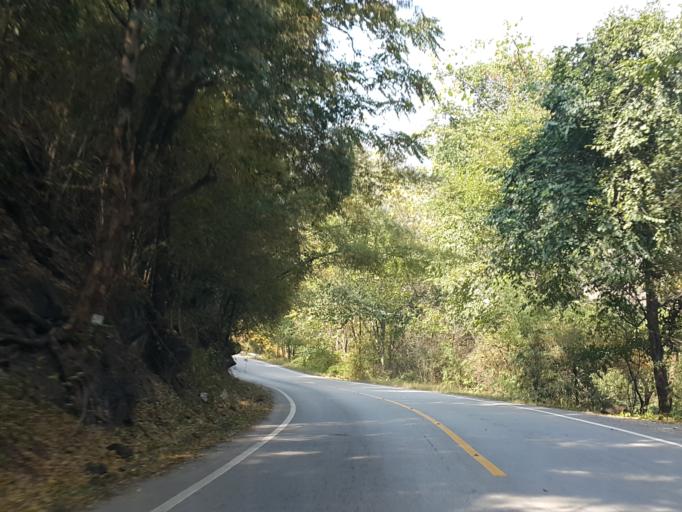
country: TH
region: Chiang Mai
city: Hot
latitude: 18.2257
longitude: 98.4960
